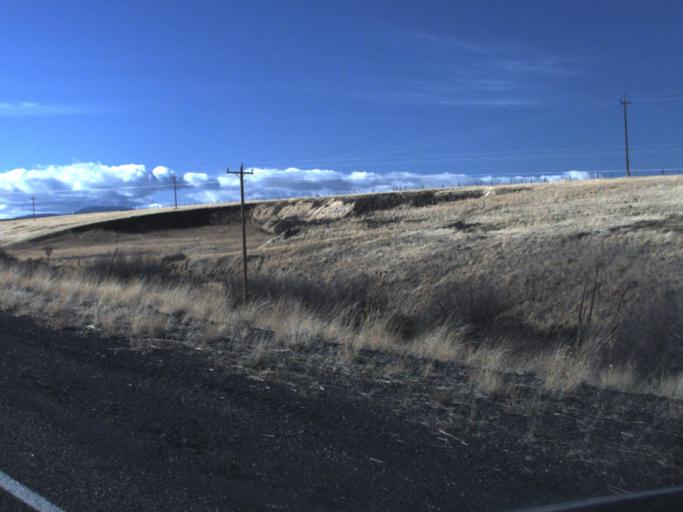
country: US
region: Washington
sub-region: Asotin County
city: Asotin
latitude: 46.1935
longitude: -117.0735
